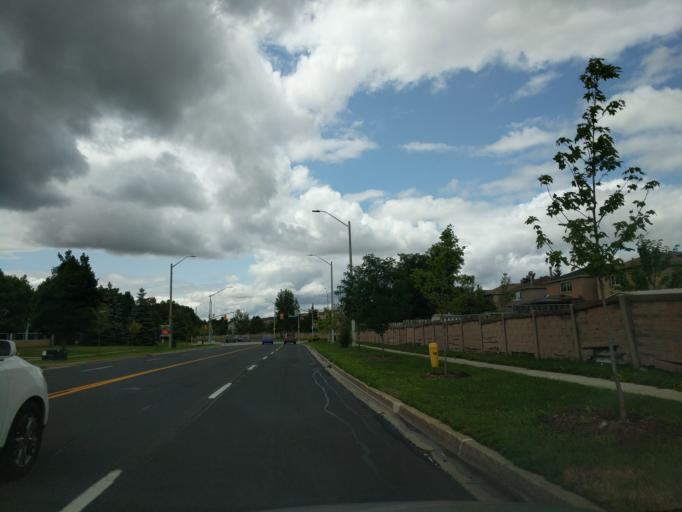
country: CA
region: Ontario
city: Markham
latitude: 43.8413
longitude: -79.2795
